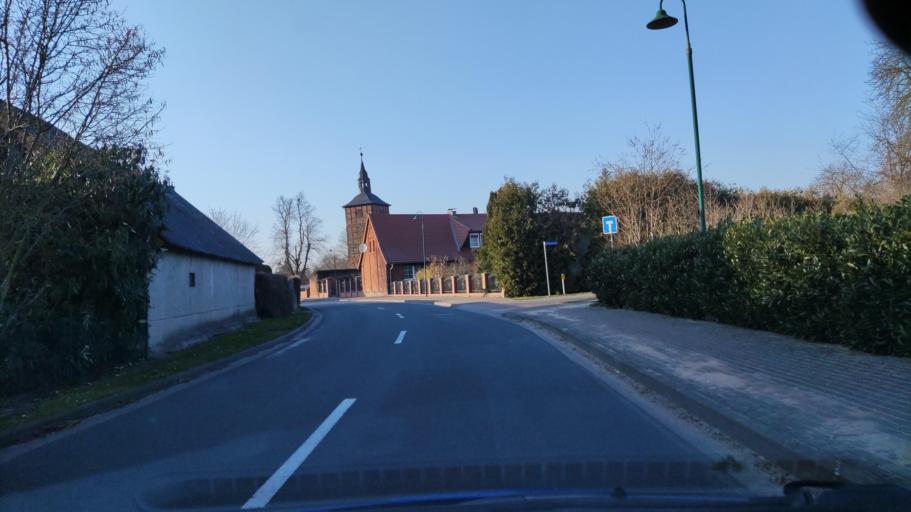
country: DE
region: Brandenburg
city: Cumlosen
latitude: 52.9682
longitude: 11.6275
